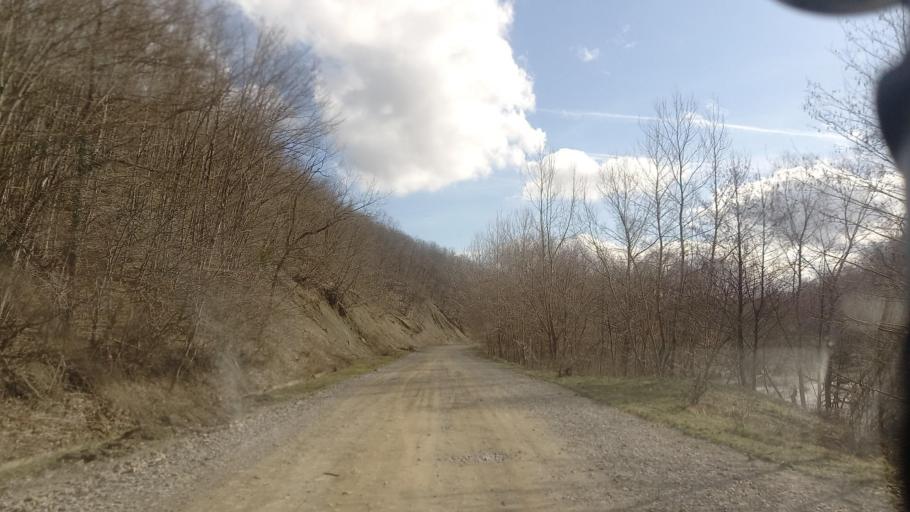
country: RU
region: Krasnodarskiy
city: Smolenskaya
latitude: 44.6095
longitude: 38.8364
